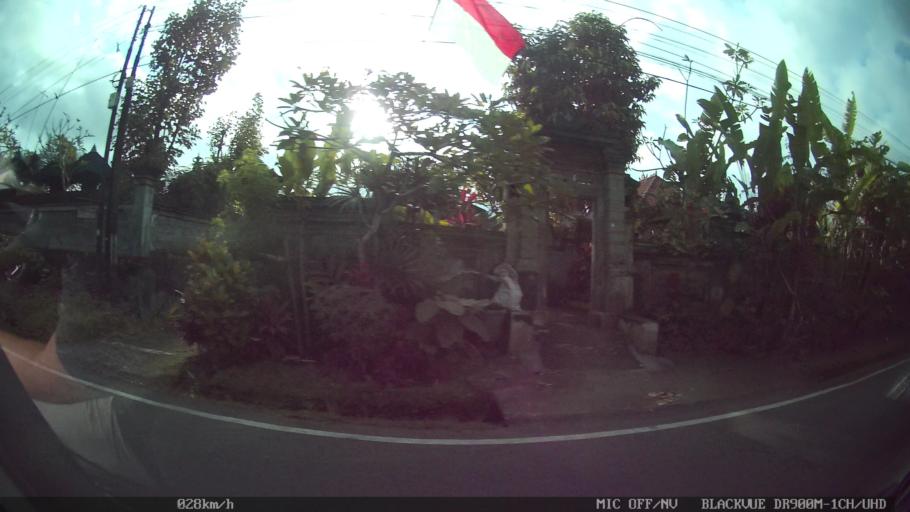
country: ID
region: Bali
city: Banjar Tebongkang
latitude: -8.5219
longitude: 115.2496
